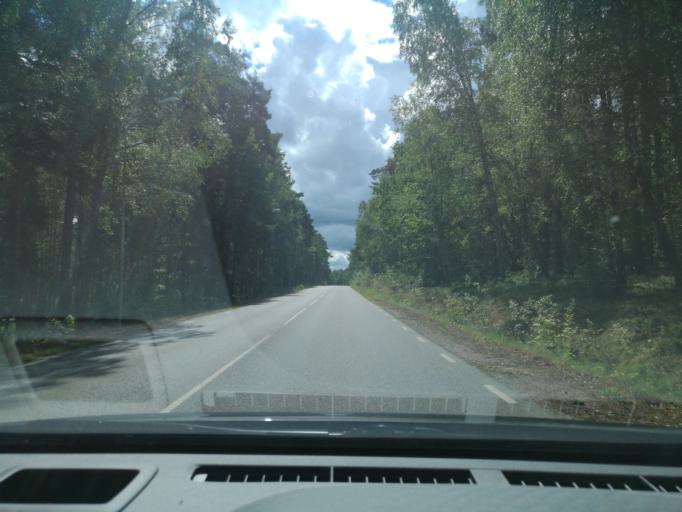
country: SE
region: Vaestmanland
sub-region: Kungsors Kommun
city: Kungsoer
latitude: 59.4172
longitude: 16.1036
